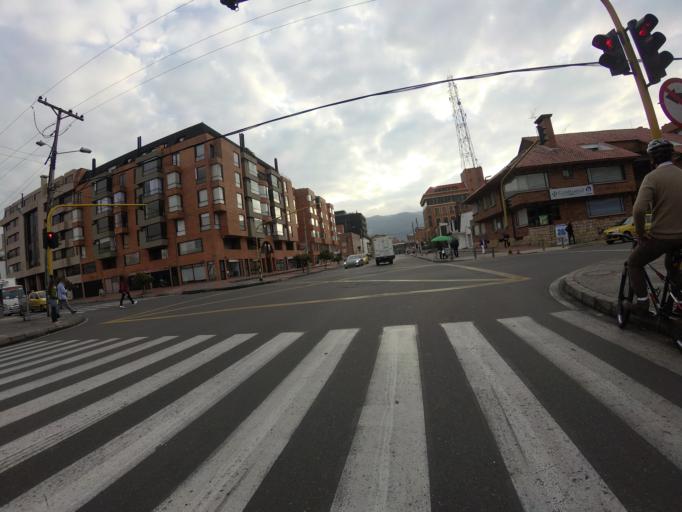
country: CO
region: Bogota D.C.
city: Barrio San Luis
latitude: 4.7048
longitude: -74.0507
